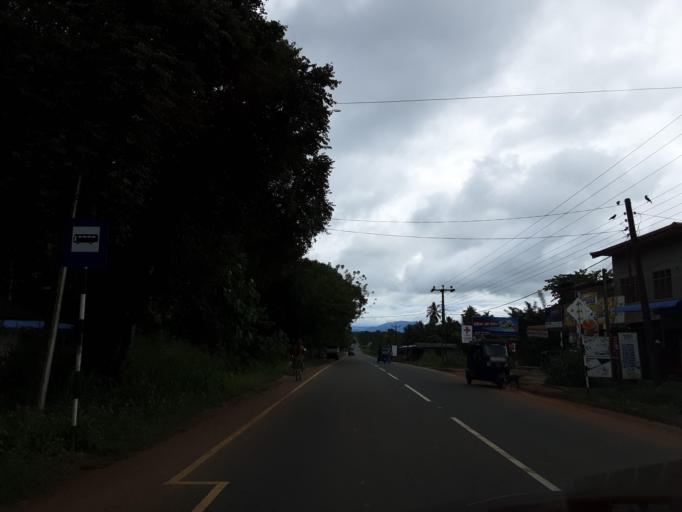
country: LK
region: Uva
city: Badulla
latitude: 7.3782
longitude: 81.0695
